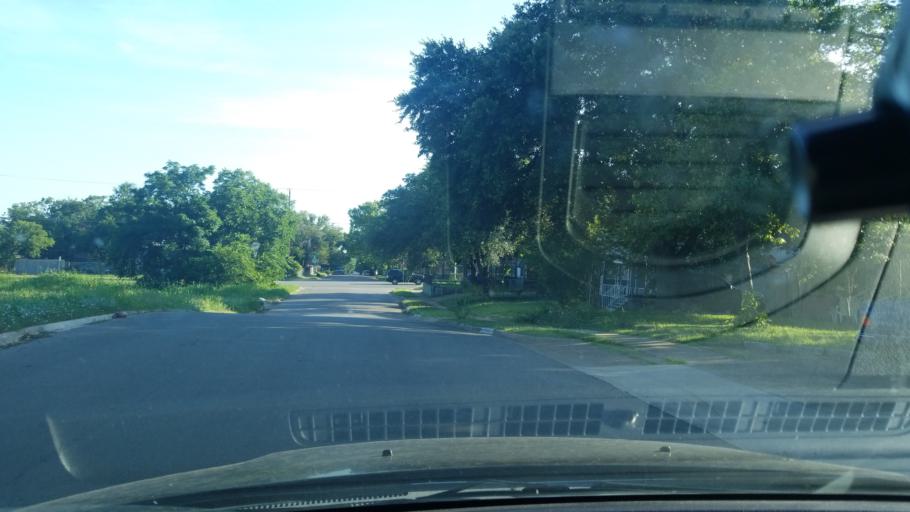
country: US
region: Texas
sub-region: Dallas County
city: Dallas
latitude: 32.7194
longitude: -96.8170
